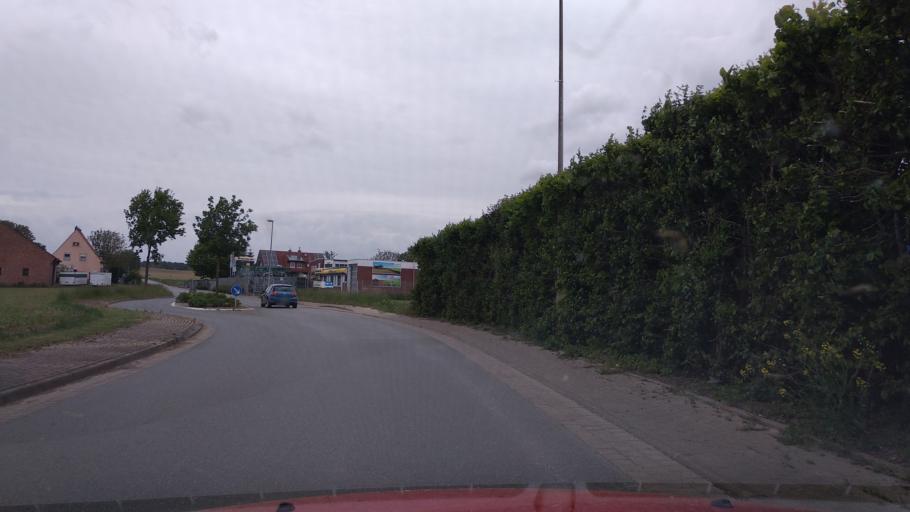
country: DE
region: North Rhine-Westphalia
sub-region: Regierungsbezirk Detmold
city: Willebadessen
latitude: 51.6023
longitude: 9.1279
